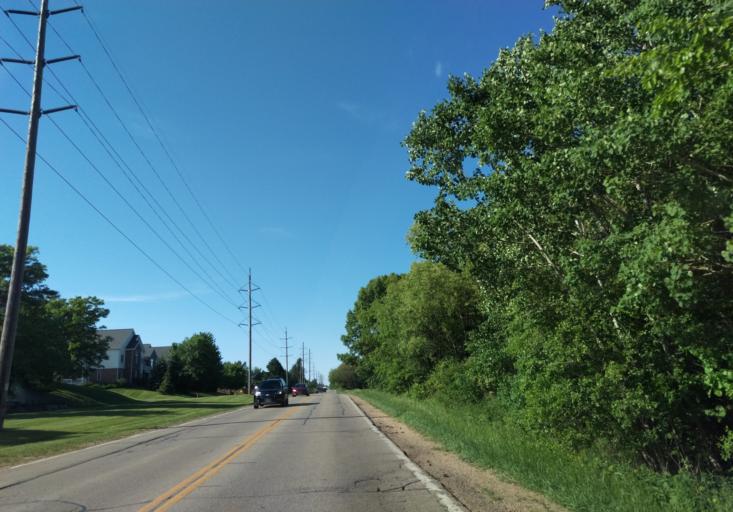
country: US
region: Wisconsin
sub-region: Dane County
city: Middleton
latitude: 43.0804
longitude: -89.5368
